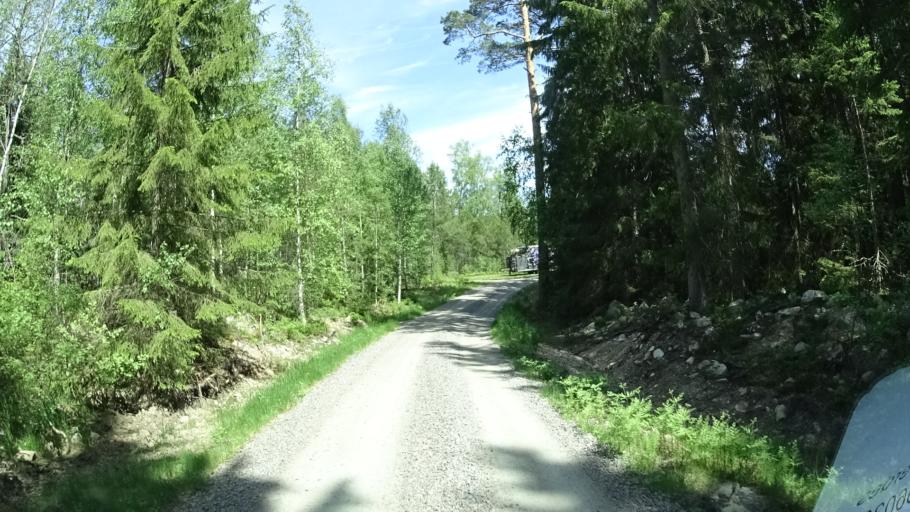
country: SE
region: OEstergoetland
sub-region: Finspangs Kommun
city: Finspang
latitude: 58.7852
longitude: 15.8970
